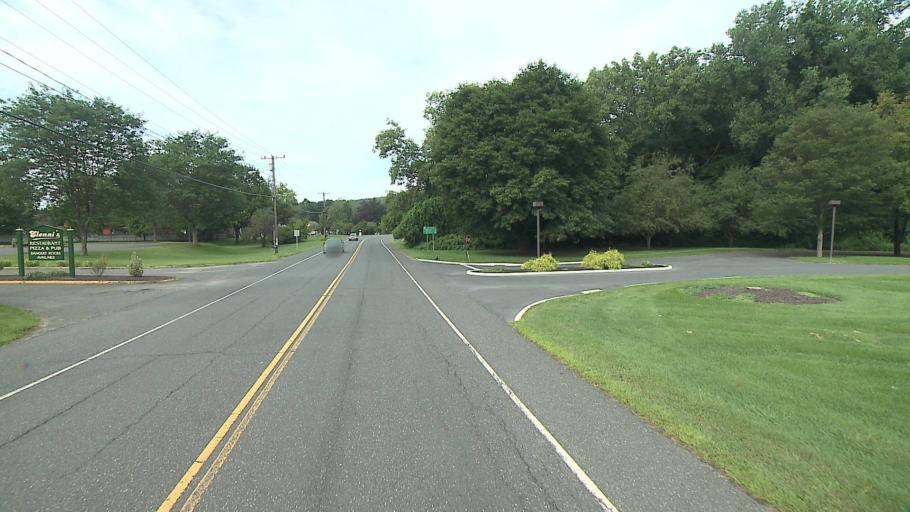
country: US
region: Connecticut
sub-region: Litchfield County
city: Woodbury Center
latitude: 41.5285
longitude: -73.2010
